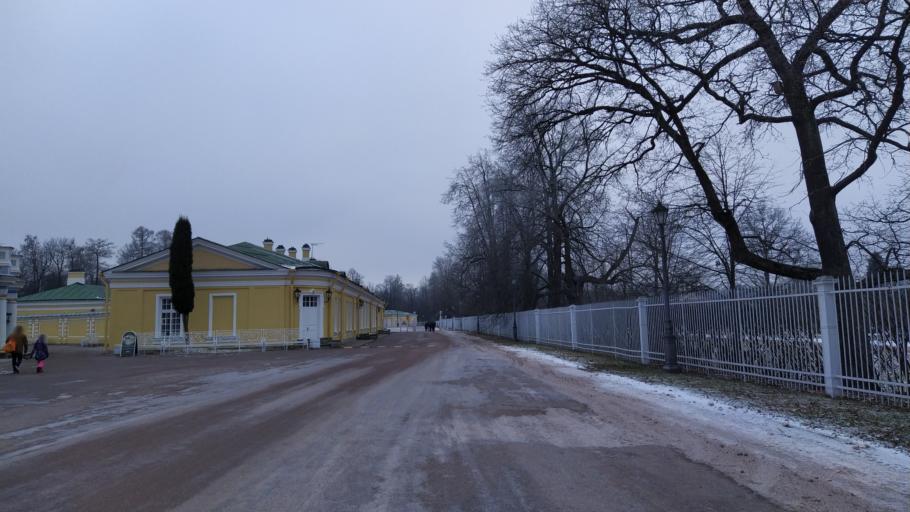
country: RU
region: St.-Petersburg
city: Pushkin
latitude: 59.7168
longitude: 30.3925
